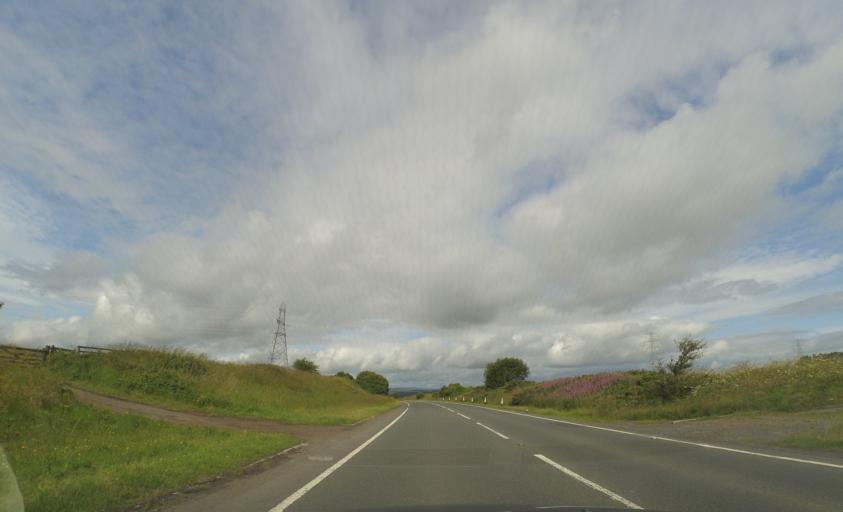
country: GB
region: Scotland
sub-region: The Scottish Borders
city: Hawick
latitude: 55.4723
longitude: -2.7963
